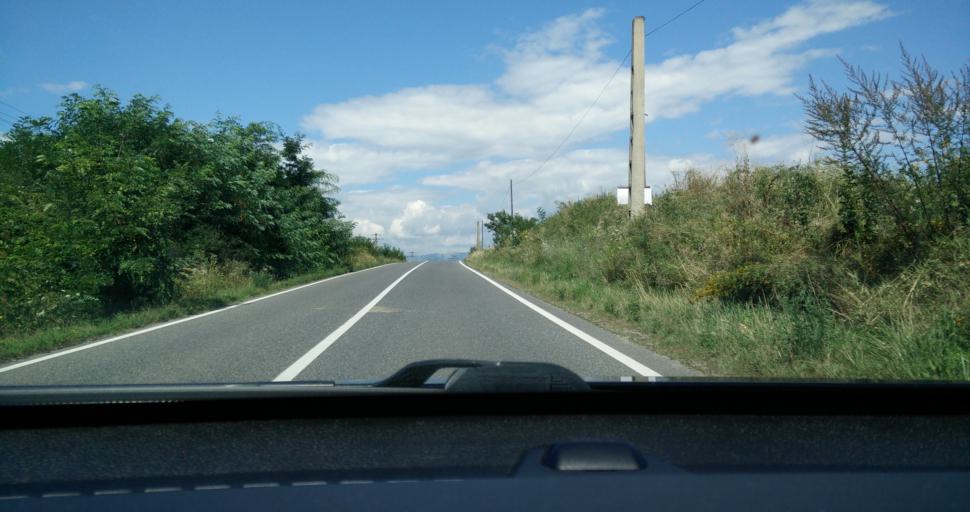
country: RO
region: Alba
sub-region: Comuna Sasciori
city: Sebesel
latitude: 45.8991
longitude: 23.5597
